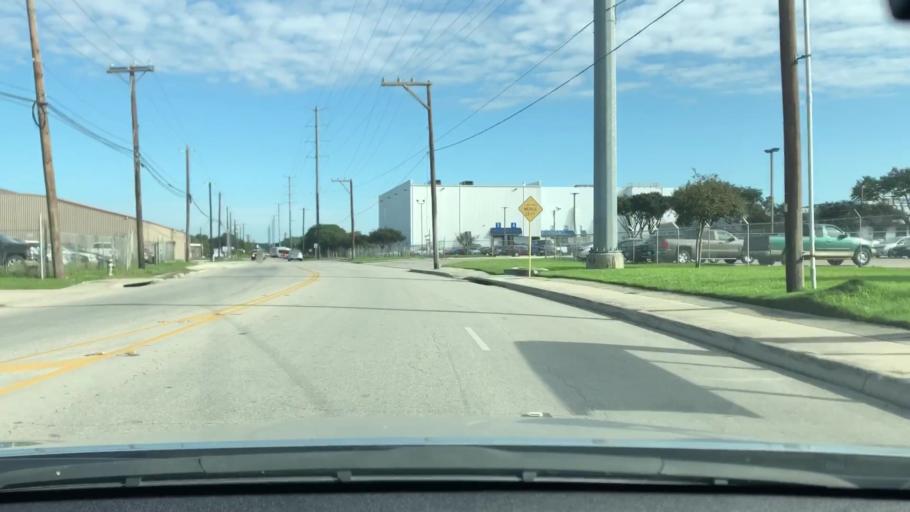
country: US
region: Texas
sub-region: Bexar County
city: Kirby
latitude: 29.4849
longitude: -98.3927
